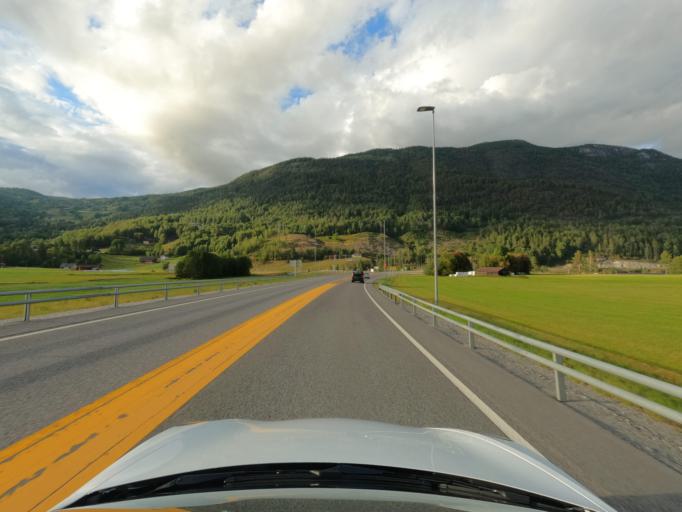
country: NO
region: Telemark
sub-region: Seljord
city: Seljord
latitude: 59.6009
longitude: 8.7151
